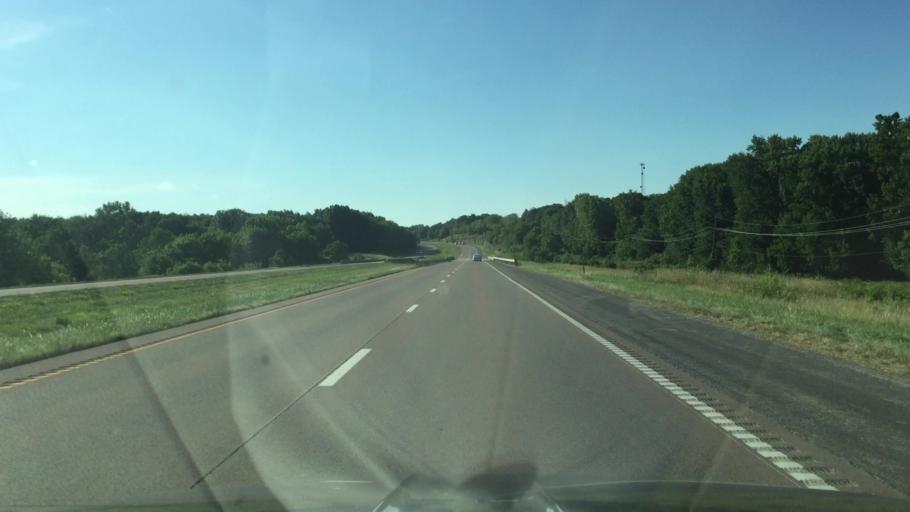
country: US
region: Missouri
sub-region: Pettis County
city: Sedalia
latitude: 38.7266
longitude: -93.3035
